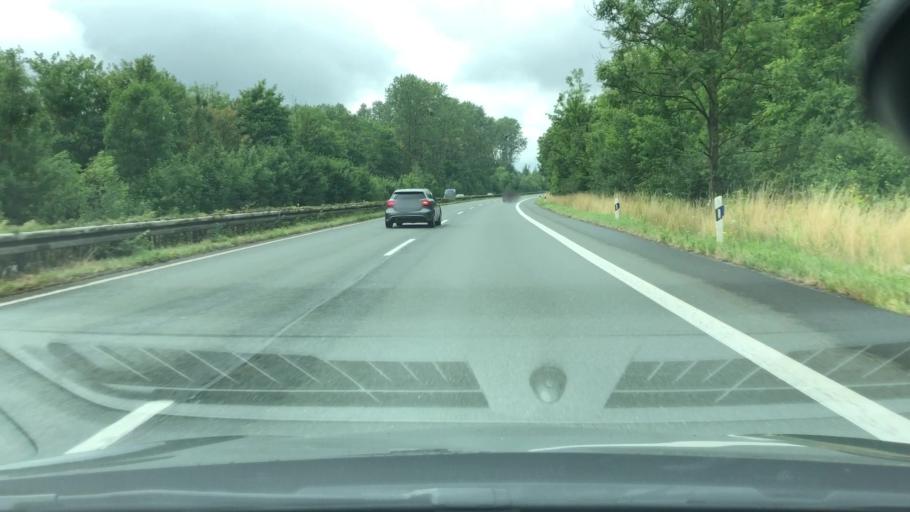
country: DE
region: Lower Saxony
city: Buckeburg
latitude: 52.2625
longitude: 8.9835
